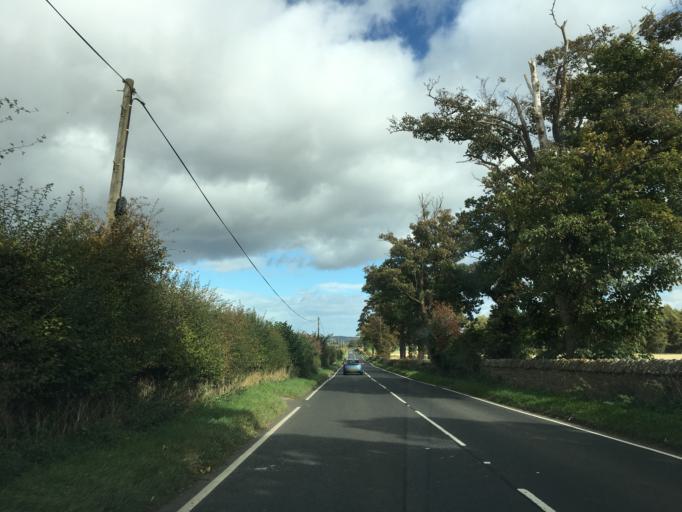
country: GB
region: Scotland
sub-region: Fife
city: Pathhead
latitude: 55.8868
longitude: -2.9816
